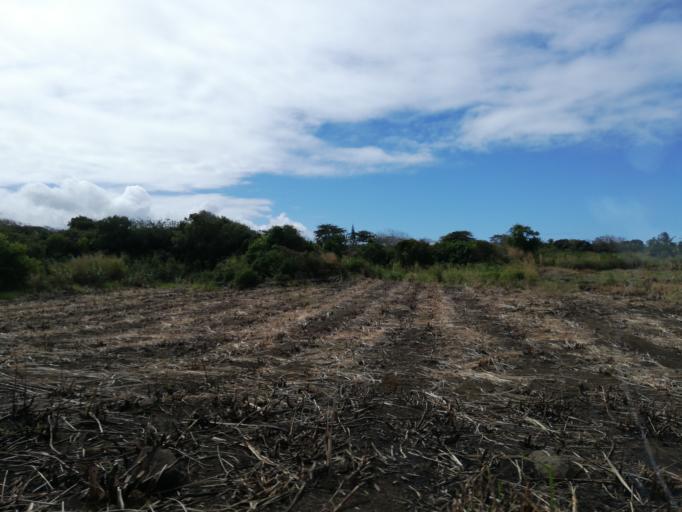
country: MU
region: Grand Port
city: Plaine Magnien
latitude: -20.4663
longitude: 57.6733
